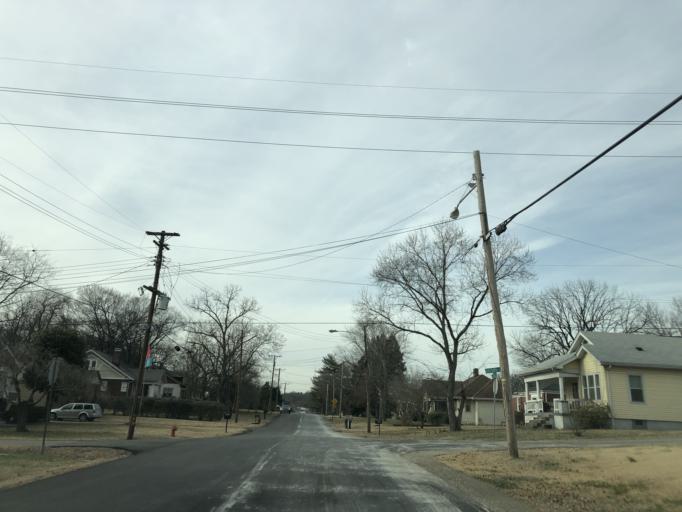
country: US
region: Tennessee
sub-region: Davidson County
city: Nashville
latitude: 36.2125
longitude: -86.7248
